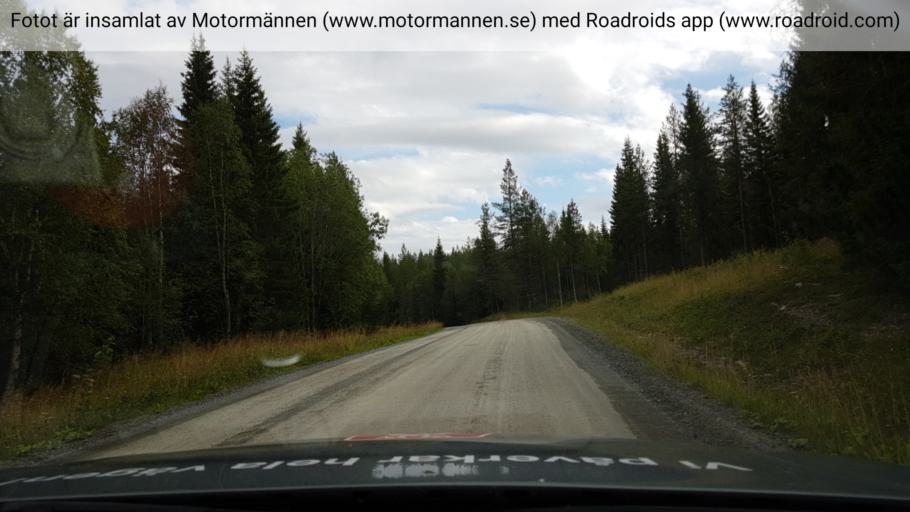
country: SE
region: Jaemtland
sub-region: Krokoms Kommun
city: Valla
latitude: 63.6653
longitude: 13.7190
